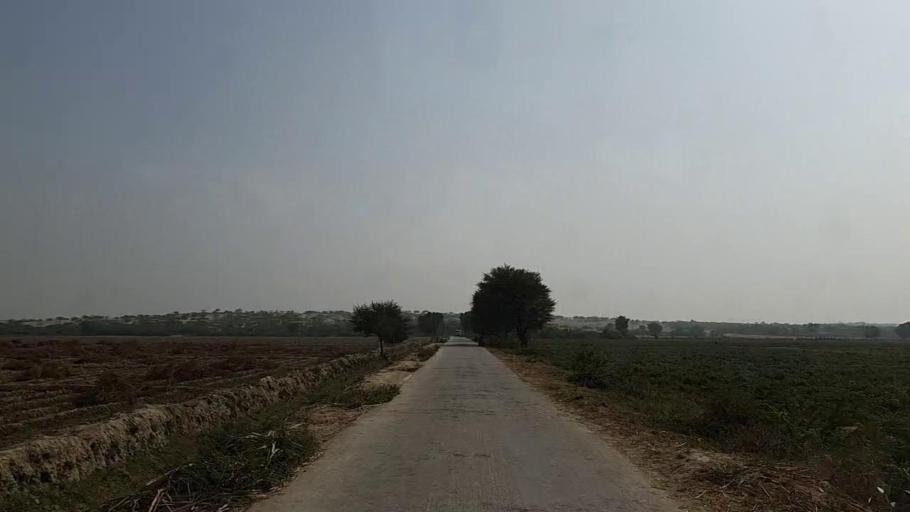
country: PK
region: Sindh
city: Naukot
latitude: 24.7501
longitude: 69.3472
